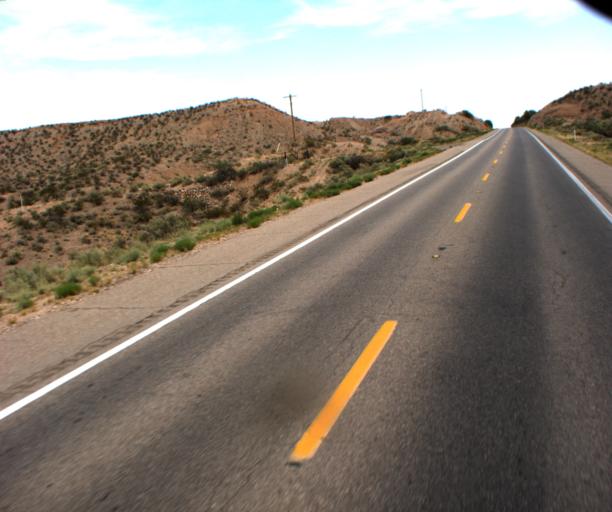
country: US
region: Arizona
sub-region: Graham County
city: Bylas
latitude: 33.0803
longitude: -110.0428
